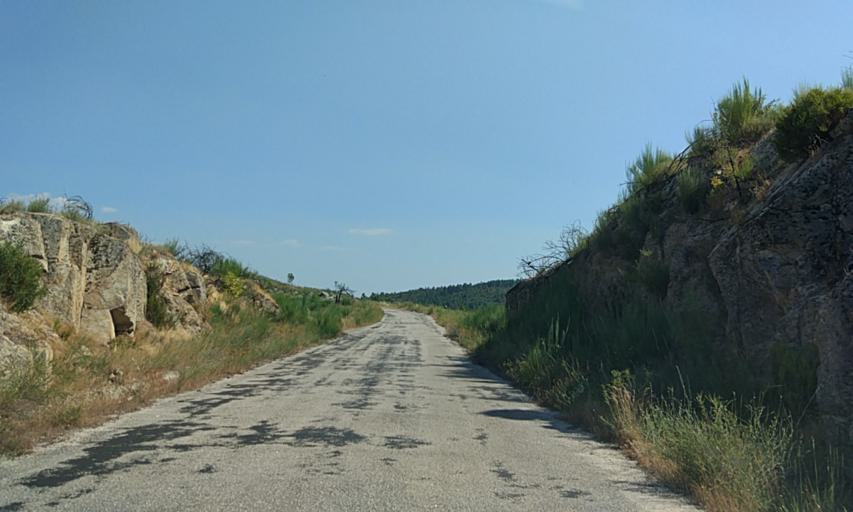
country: PT
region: Vila Real
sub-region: Sabrosa
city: Sabrosa
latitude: 41.3039
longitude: -7.4861
